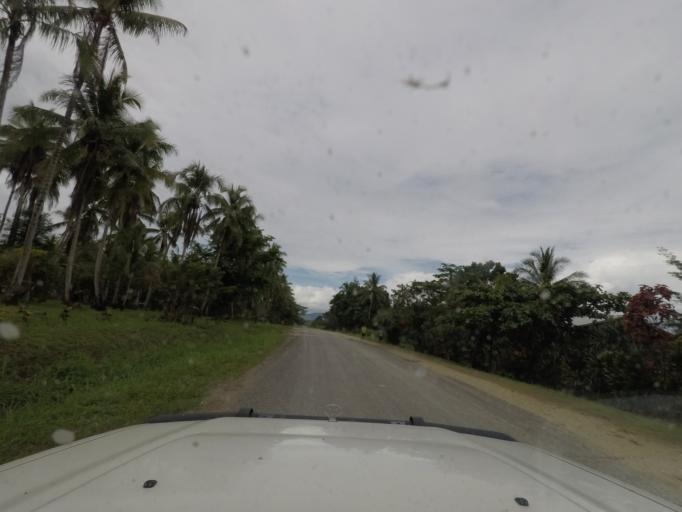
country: PG
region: Eastern Highlands
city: Goroka
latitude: -5.6734
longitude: 145.4999
